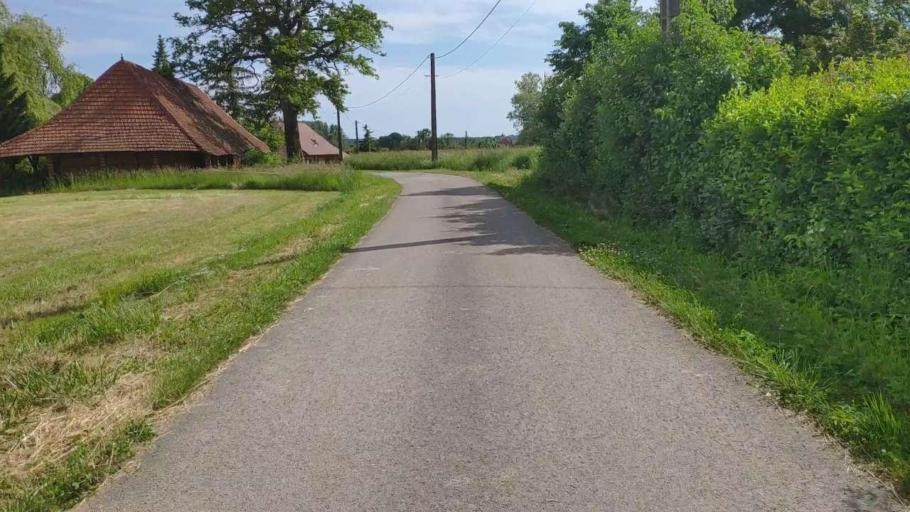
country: FR
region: Franche-Comte
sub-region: Departement du Jura
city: Bletterans
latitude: 46.8113
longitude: 5.3852
